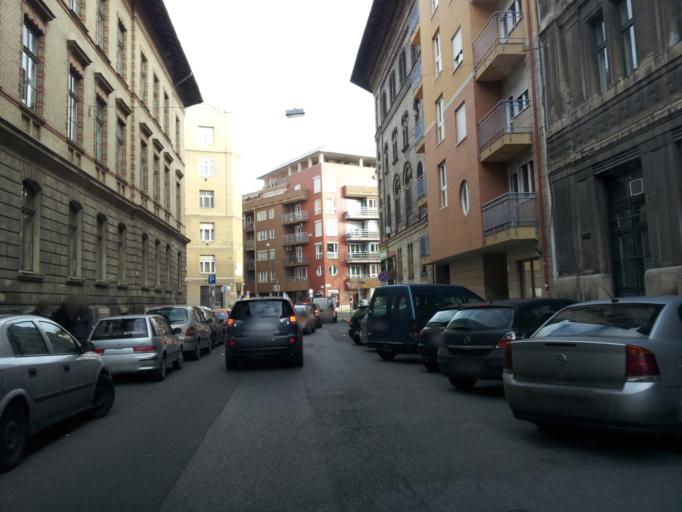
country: HU
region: Budapest
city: Budapest IX. keruelet
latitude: 47.4790
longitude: 19.0720
